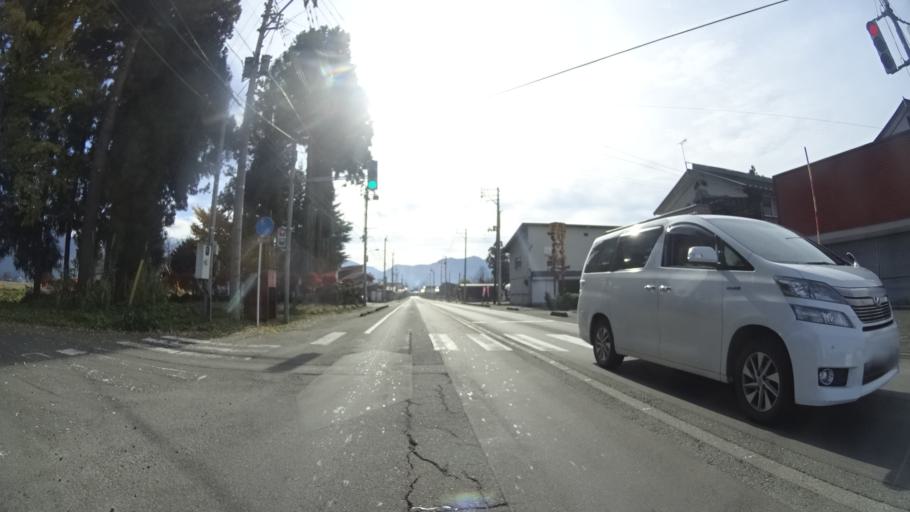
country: JP
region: Niigata
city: Muikamachi
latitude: 37.1022
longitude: 138.9201
